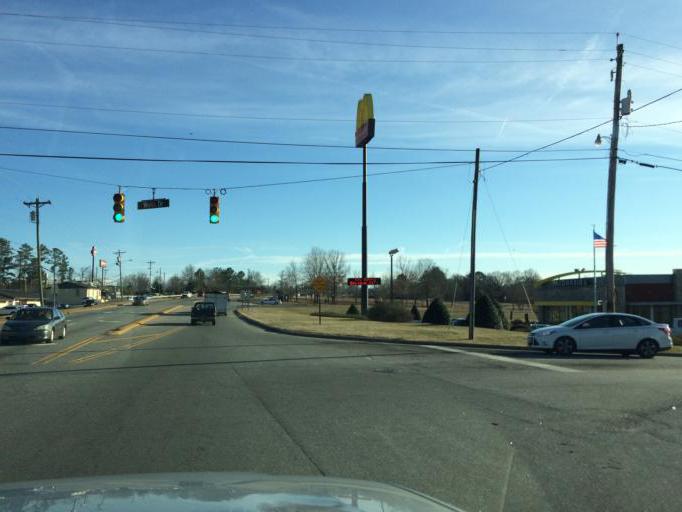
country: US
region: North Carolina
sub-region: Rutherford County
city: Forest City
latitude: 35.3177
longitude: -81.8578
